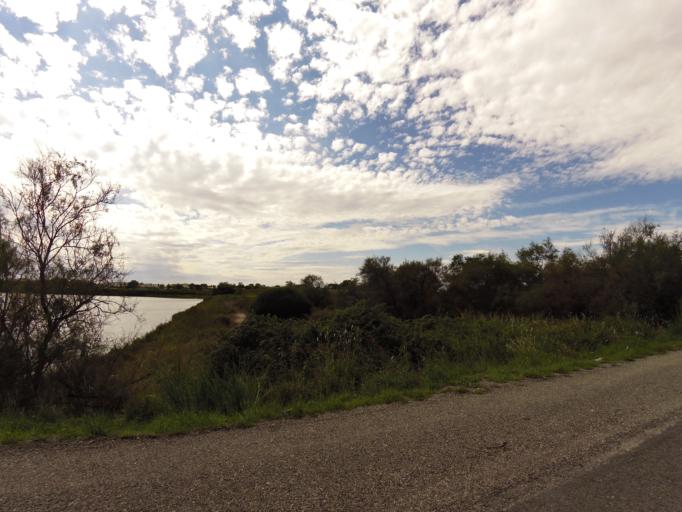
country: FR
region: Languedoc-Roussillon
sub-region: Departement du Gard
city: Le Grau-du-Roi
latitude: 43.5500
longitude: 4.1403
